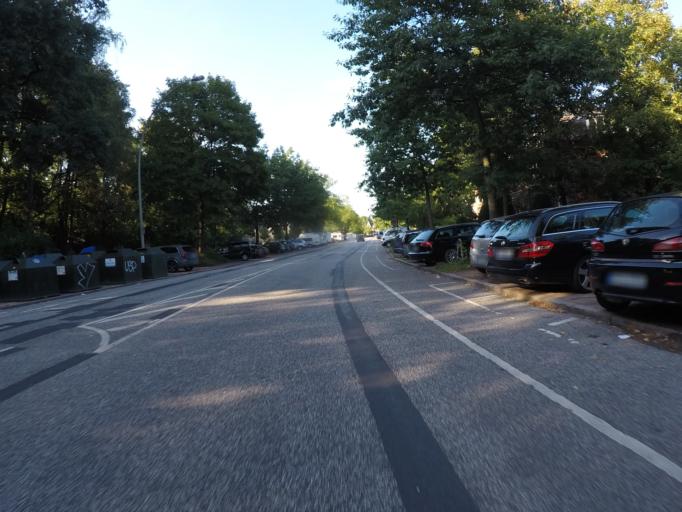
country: DE
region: Hamburg
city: Hamburg-Nord
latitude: 53.5860
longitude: 9.9888
